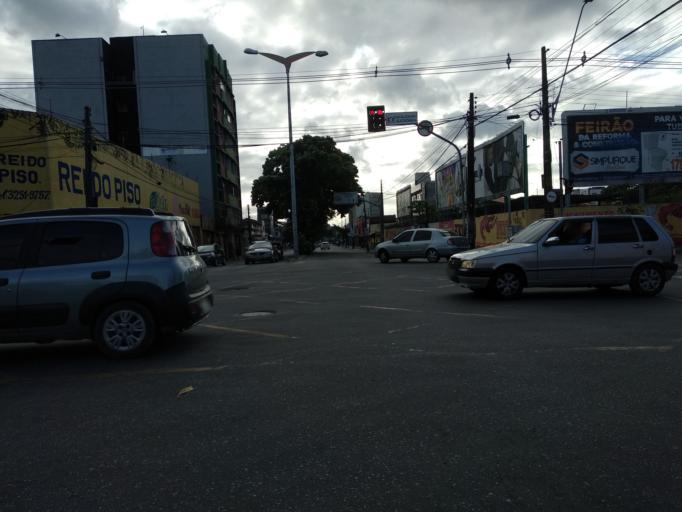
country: BR
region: Ceara
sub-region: Fortaleza
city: Fortaleza
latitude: -3.7301
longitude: -38.5352
